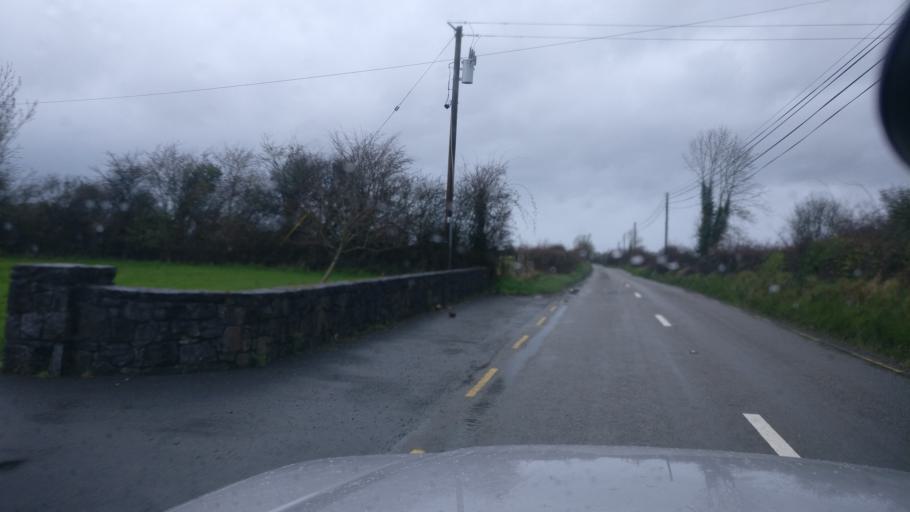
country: IE
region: Connaught
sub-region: County Galway
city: Portumna
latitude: 53.0950
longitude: -8.2677
